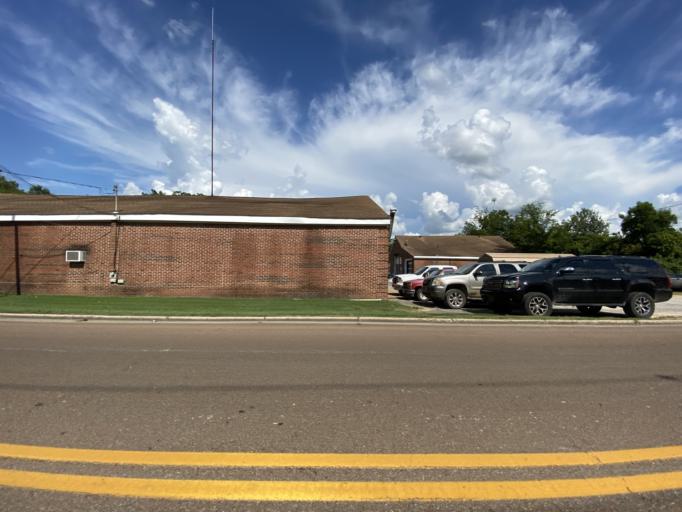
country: US
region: Tennessee
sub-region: Lauderdale County
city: Halls
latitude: 35.8729
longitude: -89.3962
